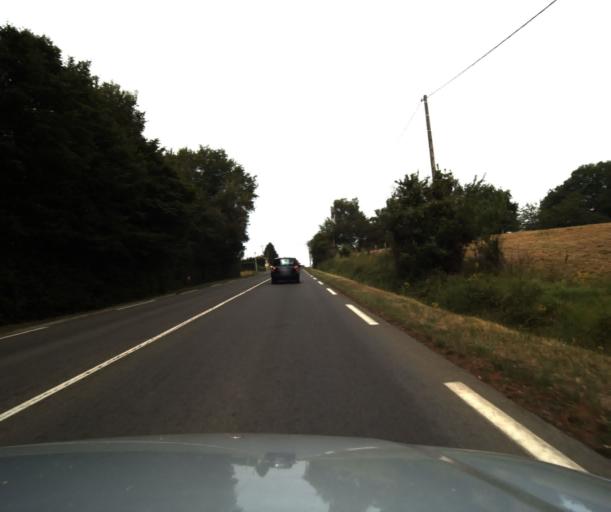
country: FR
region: Midi-Pyrenees
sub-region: Departement du Gers
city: Mielan
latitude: 43.4196
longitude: 0.2541
